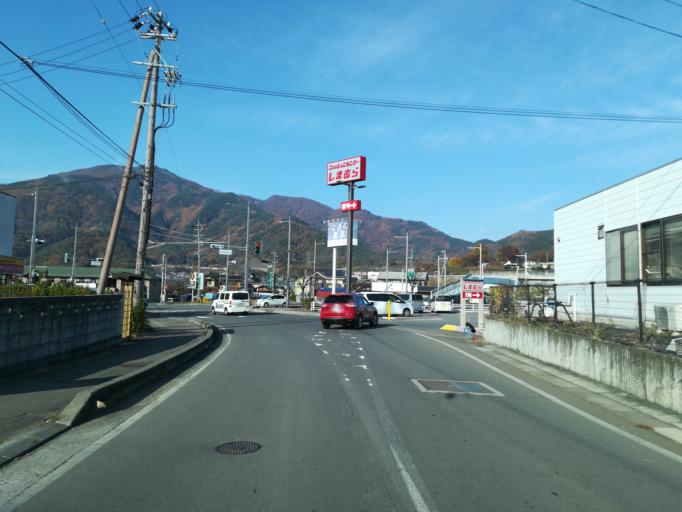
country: JP
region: Nagano
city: Ueda
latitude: 36.4065
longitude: 138.2802
